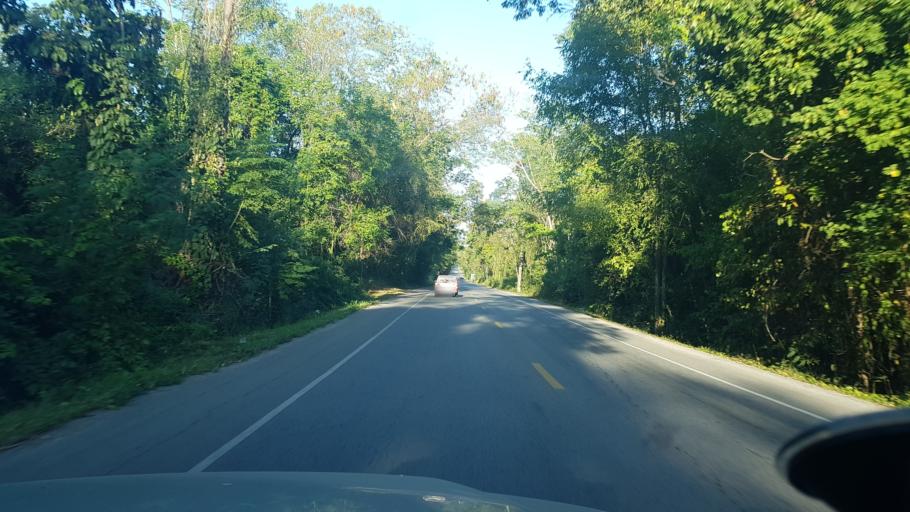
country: TH
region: Khon Kaen
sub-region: Amphoe Phu Pha Man
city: Phu Pha Man
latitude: 16.6269
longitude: 101.8487
